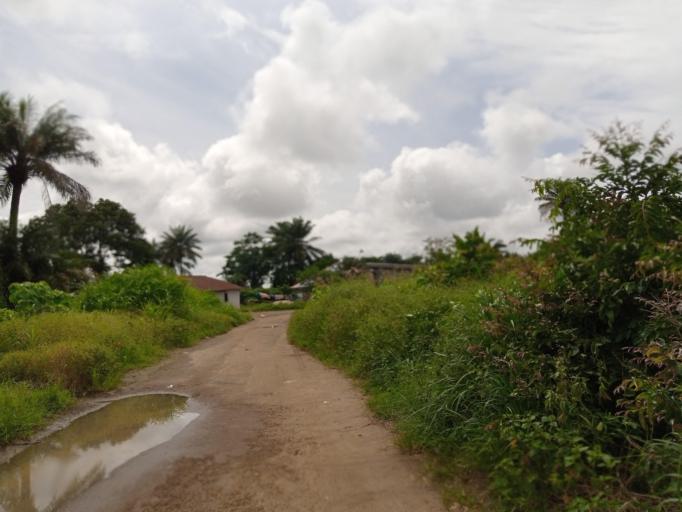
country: SL
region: Northern Province
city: Masoyila
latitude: 8.5889
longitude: -13.1963
